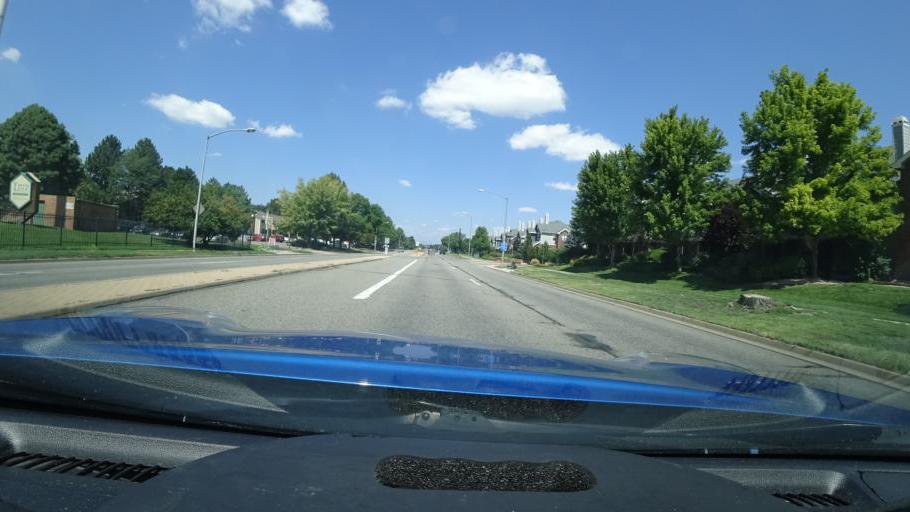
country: US
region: Colorado
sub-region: Arapahoe County
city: Glendale
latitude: 39.7079
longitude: -104.8868
